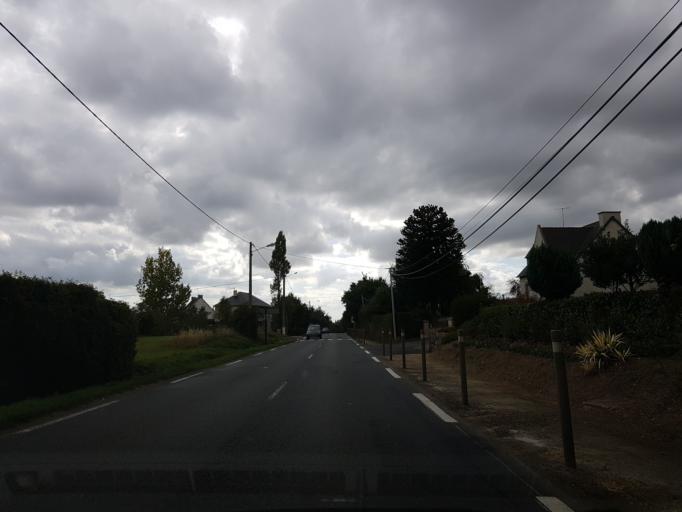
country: FR
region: Brittany
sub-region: Departement des Cotes-d'Armor
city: Pommeret
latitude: 48.4669
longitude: -2.6521
